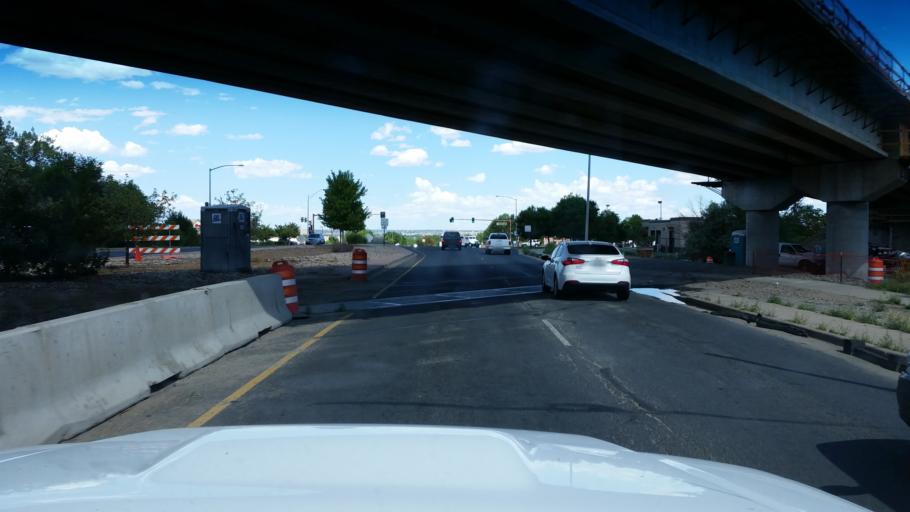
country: US
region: Colorado
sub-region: Adams County
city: Thornton
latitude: 39.8848
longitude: -104.9466
